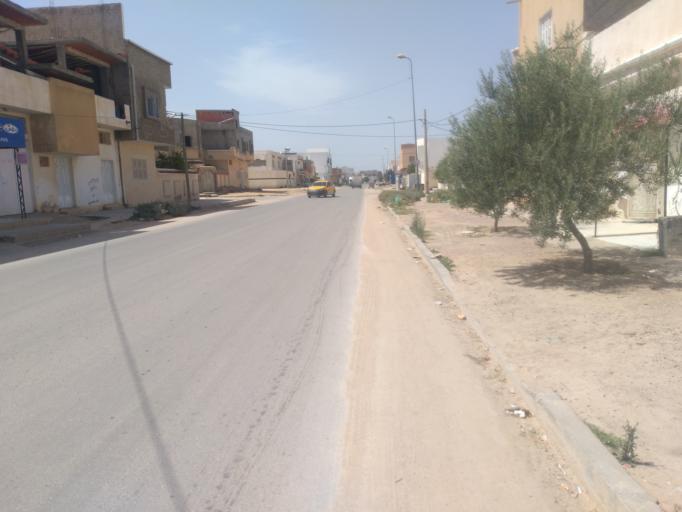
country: TN
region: Al Qayrawan
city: Kairouan
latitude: 35.6651
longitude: 10.0788
